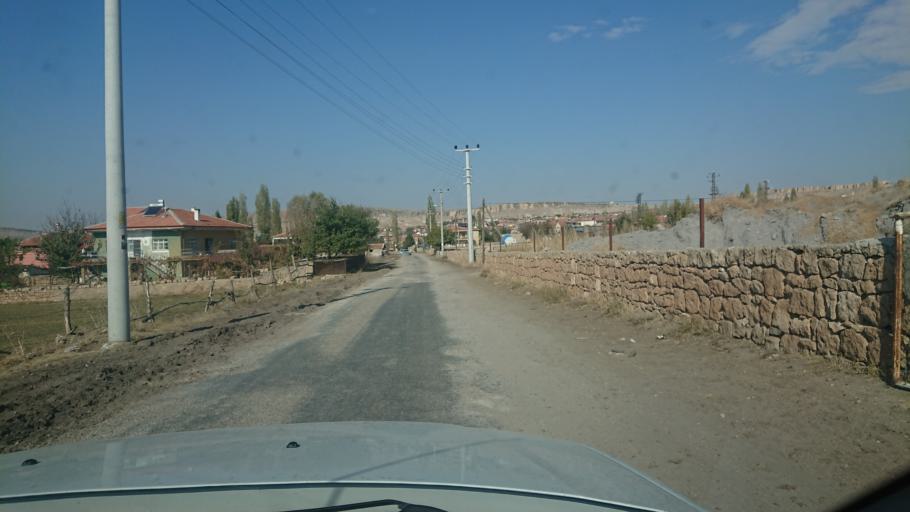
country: TR
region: Aksaray
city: Gulagac
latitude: 38.3490
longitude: 34.2356
